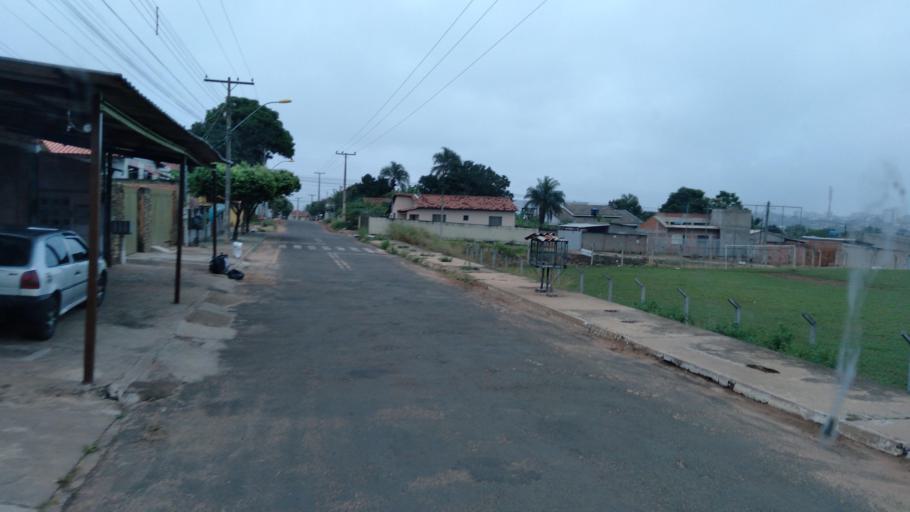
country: BR
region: Goias
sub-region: Mineiros
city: Mineiros
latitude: -17.5792
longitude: -52.5464
